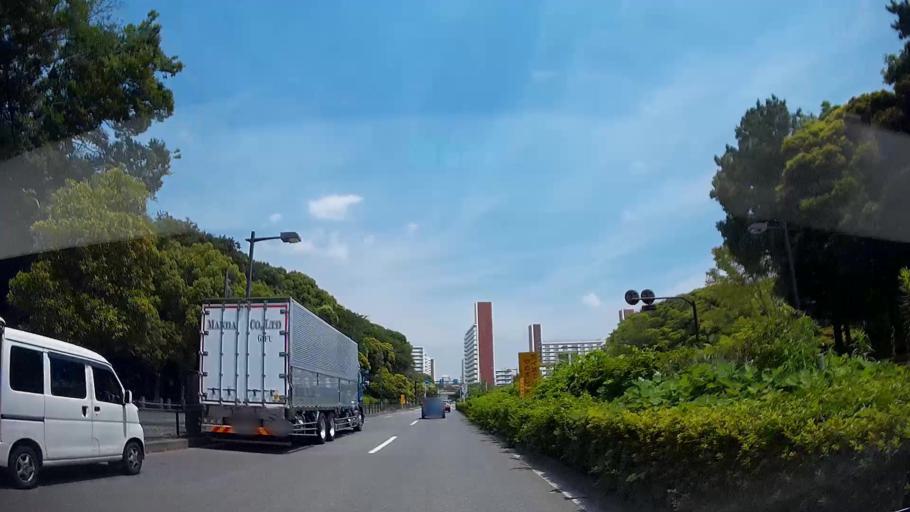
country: JP
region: Kanagawa
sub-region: Kawasaki-shi
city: Kawasaki
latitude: 35.5939
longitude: 139.7510
